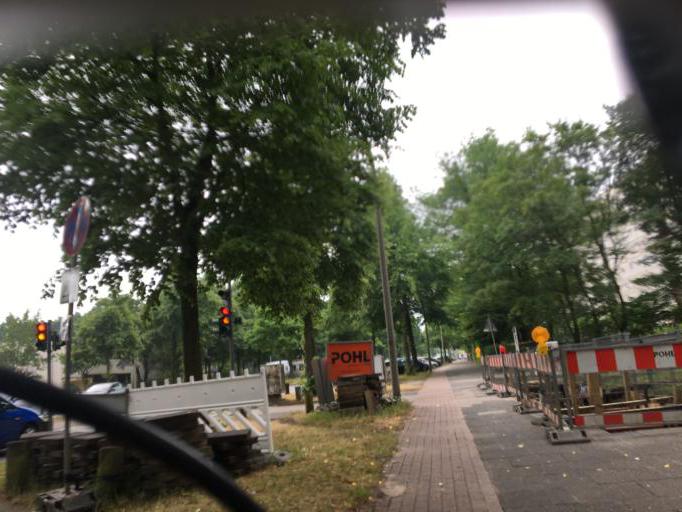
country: DE
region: Schleswig-Holstein
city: Halstenbek
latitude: 53.5911
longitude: 9.8523
